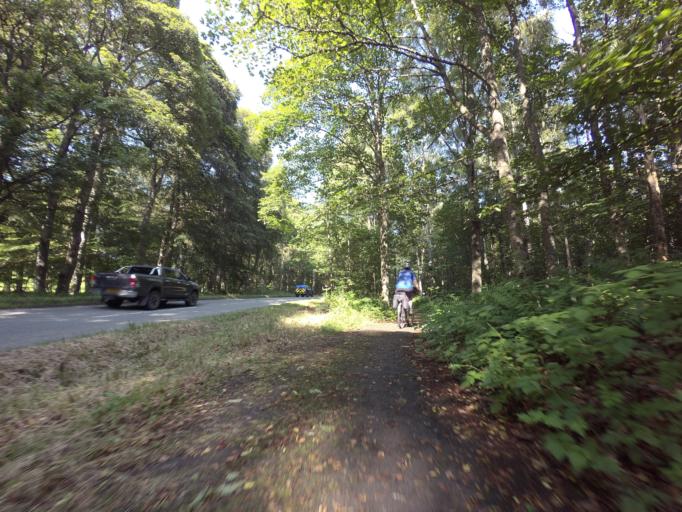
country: GB
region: Scotland
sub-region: Highland
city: Evanton
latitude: 57.6737
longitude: -4.3189
